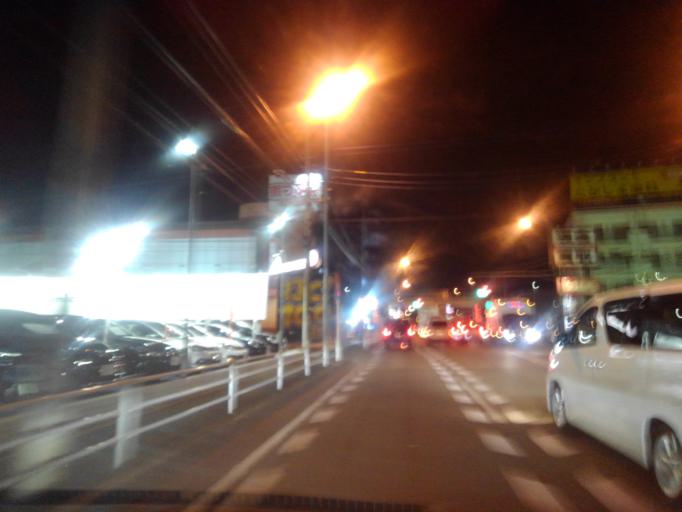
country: JP
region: Tokyo
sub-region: Machida-shi
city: Machida
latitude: 35.5590
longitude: 139.4038
